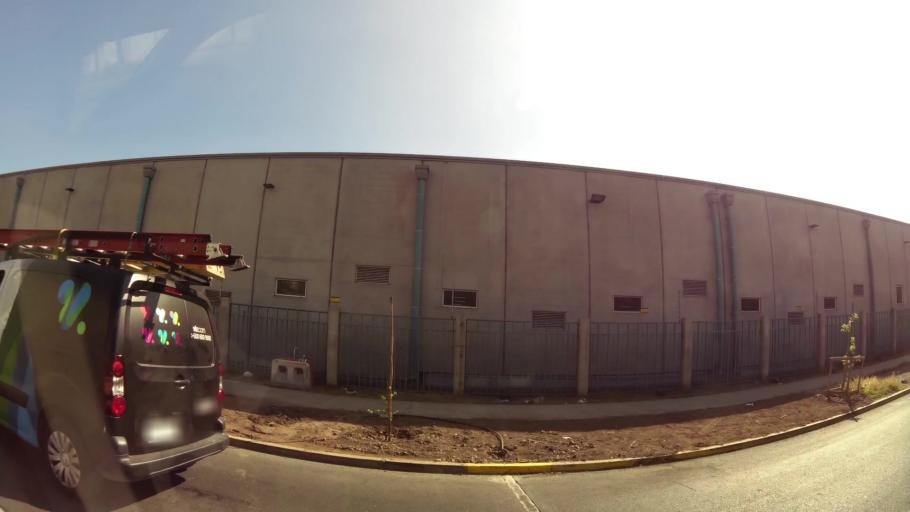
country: CL
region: Santiago Metropolitan
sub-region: Provincia de Santiago
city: Santiago
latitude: -33.4597
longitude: -70.6263
